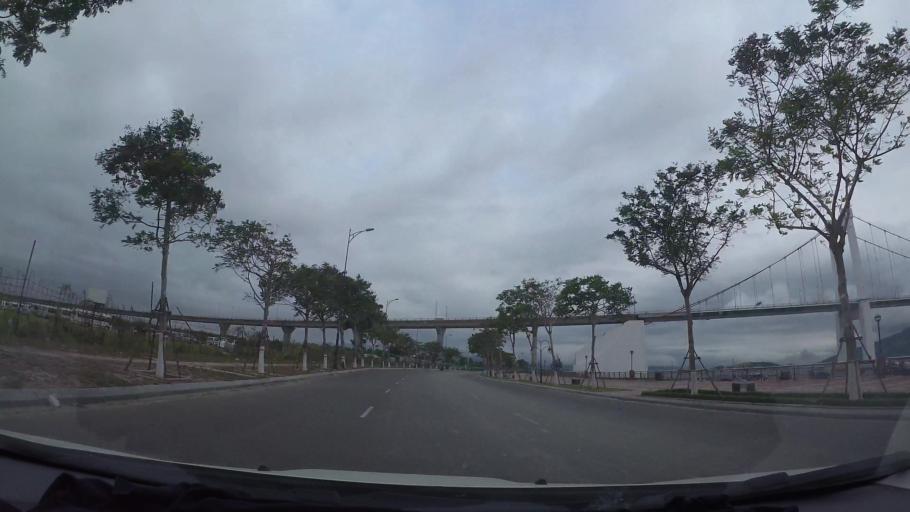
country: VN
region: Da Nang
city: Da Nang
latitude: 16.0920
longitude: 108.2184
